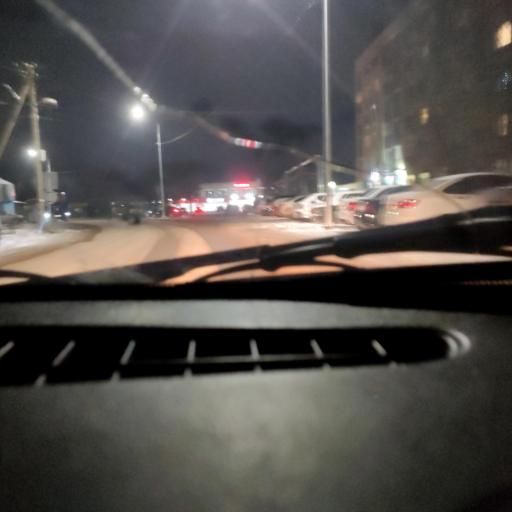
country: RU
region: Bashkortostan
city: Avdon
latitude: 54.6097
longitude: 55.8423
